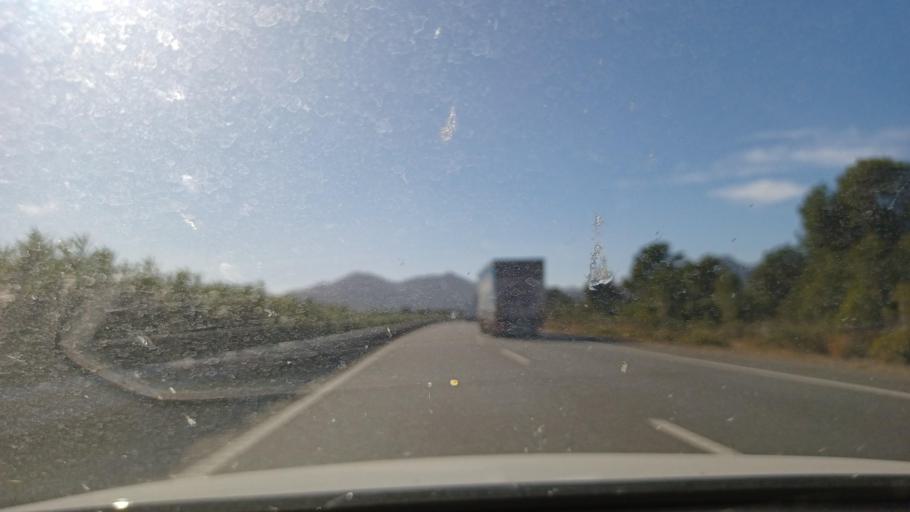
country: ES
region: Catalonia
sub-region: Provincia de Tarragona
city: Vilanova d'Escornalbou
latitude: 41.0392
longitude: 0.9520
